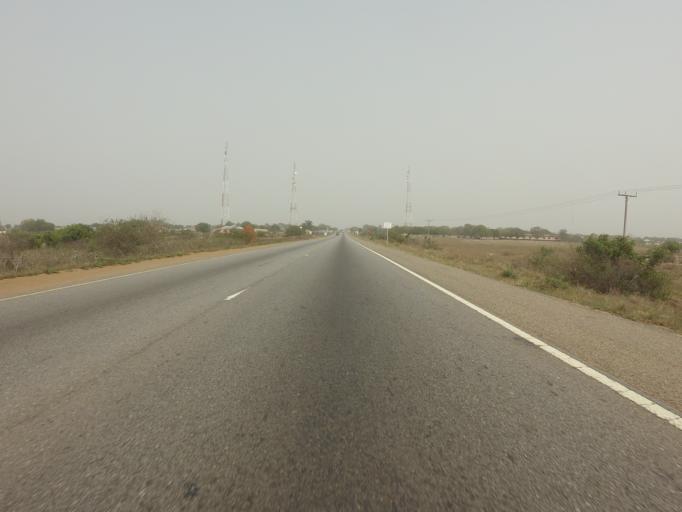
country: GH
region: Greater Accra
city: Tema
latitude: 5.8637
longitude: 0.2846
